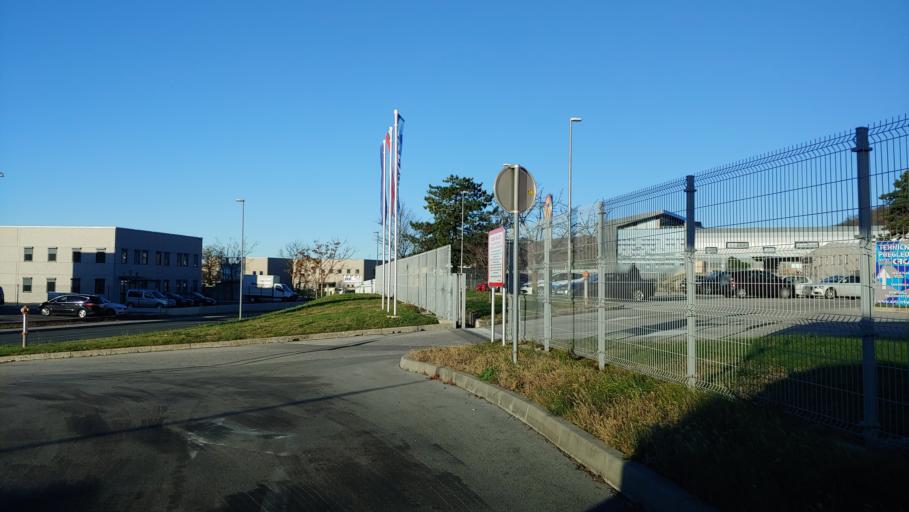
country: SI
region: Sezana
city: Sezana
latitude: 45.7093
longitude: 13.8575
